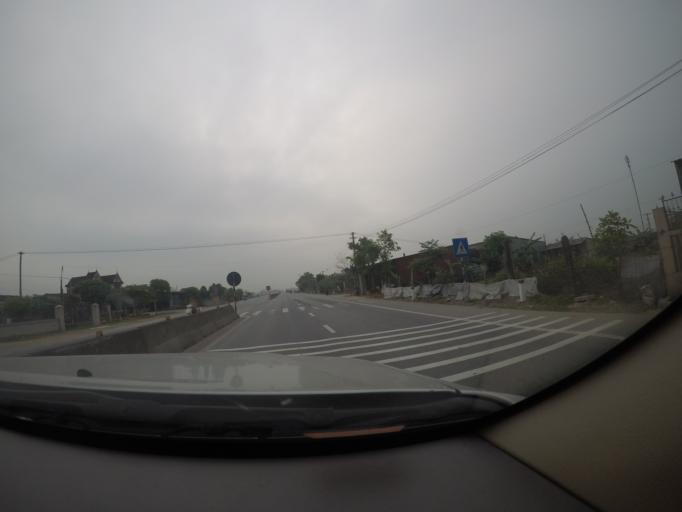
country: VN
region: Ha Tinh
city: Cam Xuyen
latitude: 18.2250
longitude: 106.0595
